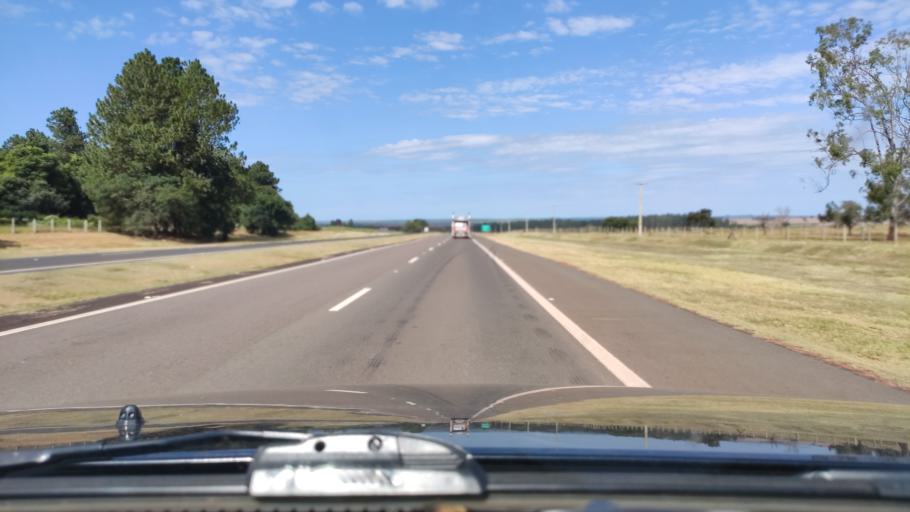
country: BR
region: Sao Paulo
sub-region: Rancharia
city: Rancharia
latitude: -22.4568
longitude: -50.9716
